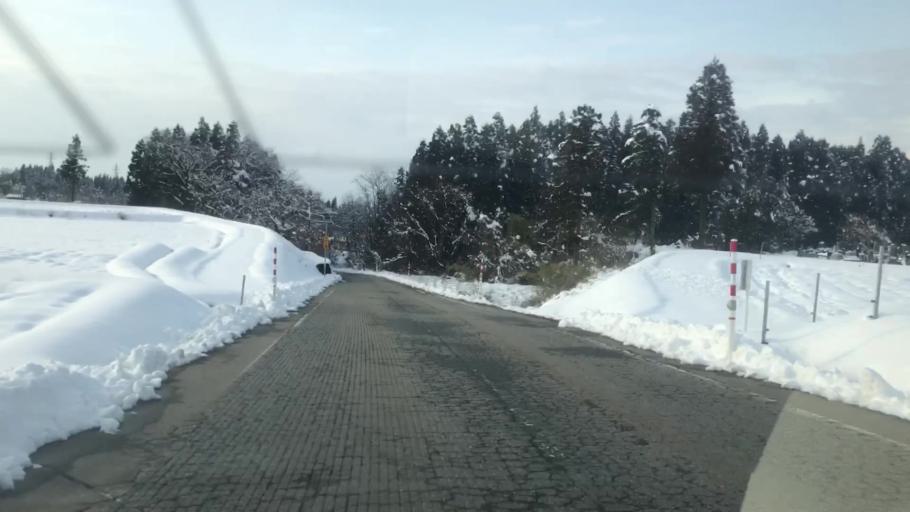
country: JP
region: Toyama
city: Kamiichi
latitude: 36.6036
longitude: 137.3074
